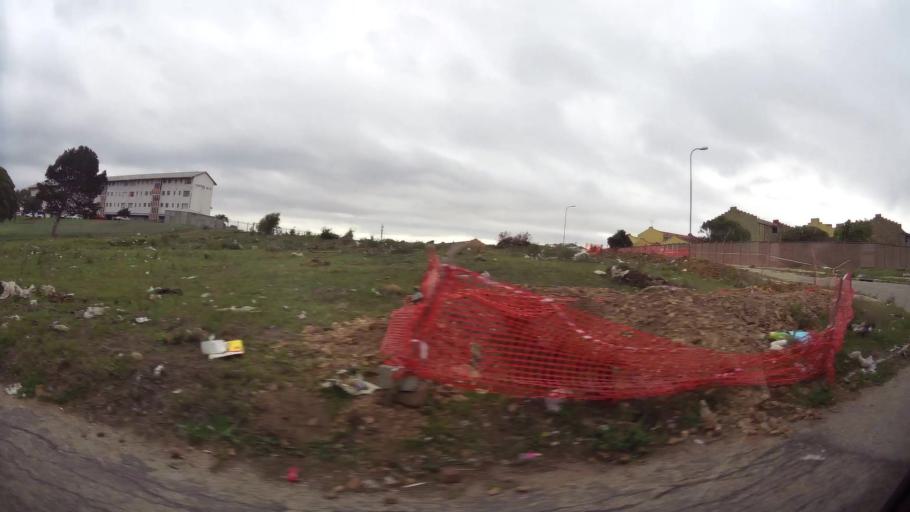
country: ZA
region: Eastern Cape
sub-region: Nelson Mandela Bay Metropolitan Municipality
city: Port Elizabeth
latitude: -33.9054
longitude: 25.5611
